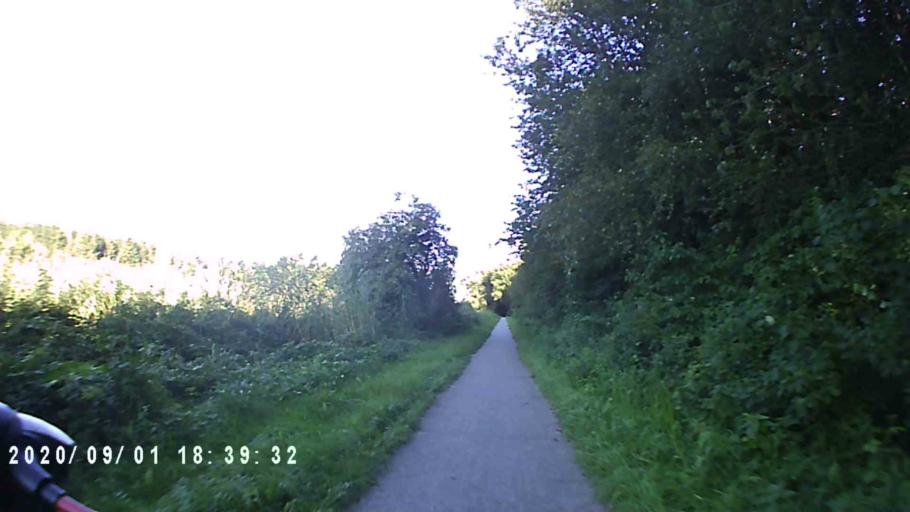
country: NL
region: Groningen
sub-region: Gemeente Hoogezand-Sappemeer
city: Sappemeer
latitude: 53.1465
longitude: 6.8184
